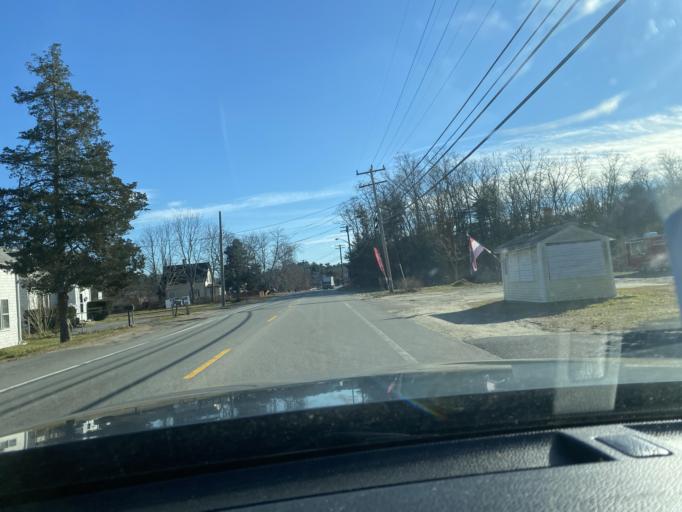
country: US
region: Massachusetts
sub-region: Plymouth County
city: West Wareham
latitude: 41.7950
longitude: -70.7599
